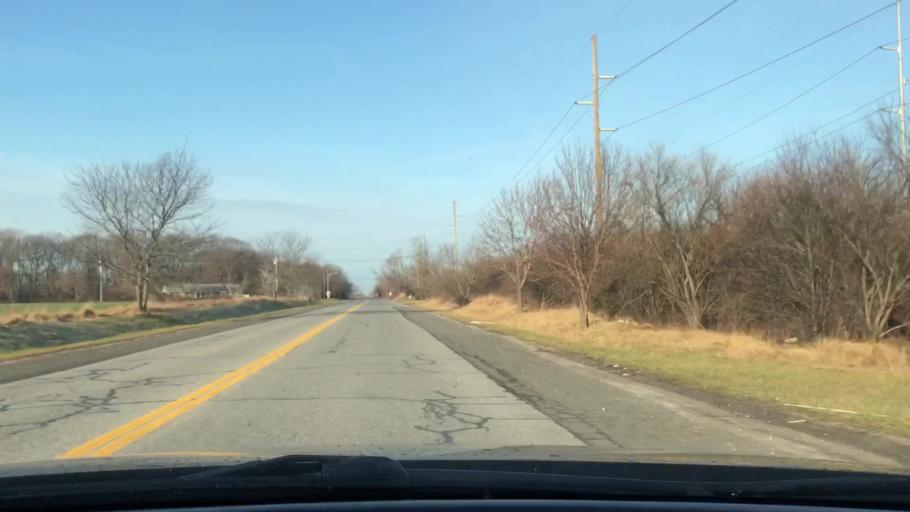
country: US
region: New York
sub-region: Suffolk County
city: Calverton
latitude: 40.9289
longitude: -72.7260
